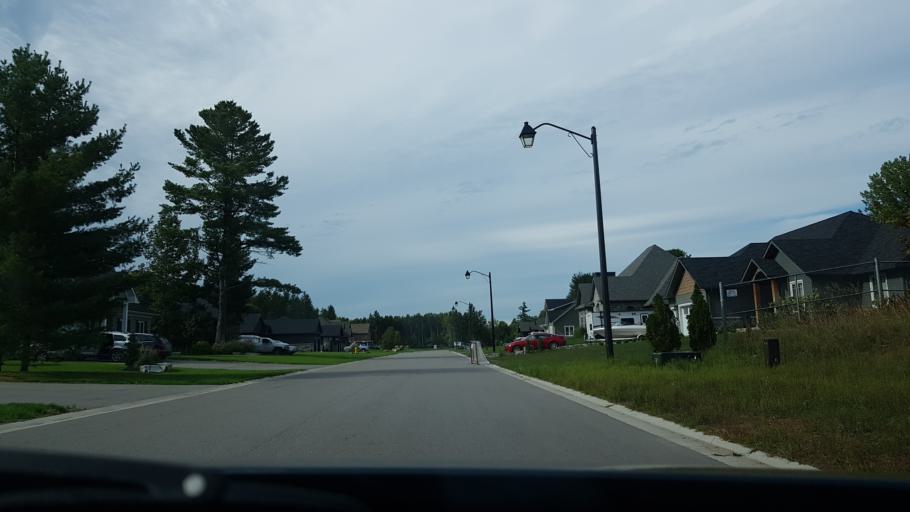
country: CA
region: Ontario
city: Angus
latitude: 44.4800
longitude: -79.8217
